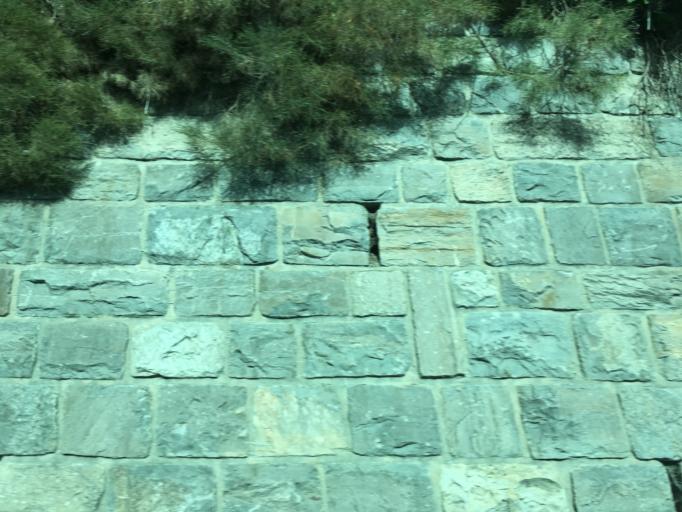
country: CH
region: Valais
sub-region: Sierre District
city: Montana
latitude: 46.3117
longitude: 7.4777
